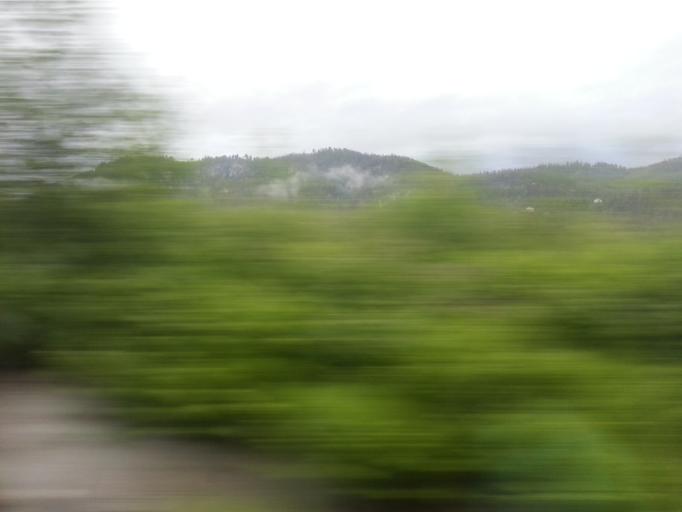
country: NO
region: Sor-Trondelag
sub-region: Midtre Gauldal
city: Storen
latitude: 63.0416
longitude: 10.2857
